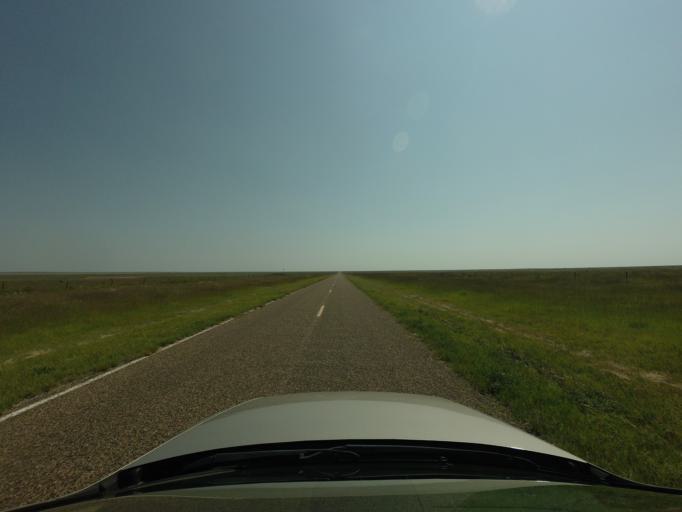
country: US
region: New Mexico
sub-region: Curry County
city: Cannon Air Force Base
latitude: 34.6334
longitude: -103.4828
